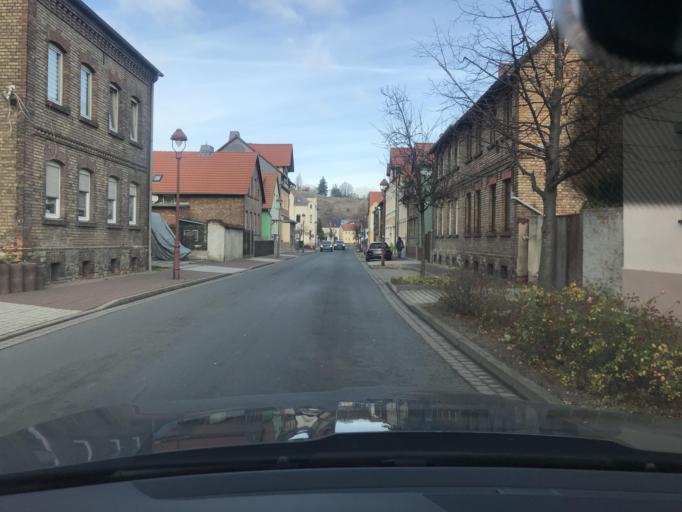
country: DE
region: Saxony-Anhalt
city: Thale
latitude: 51.7528
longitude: 11.0337
